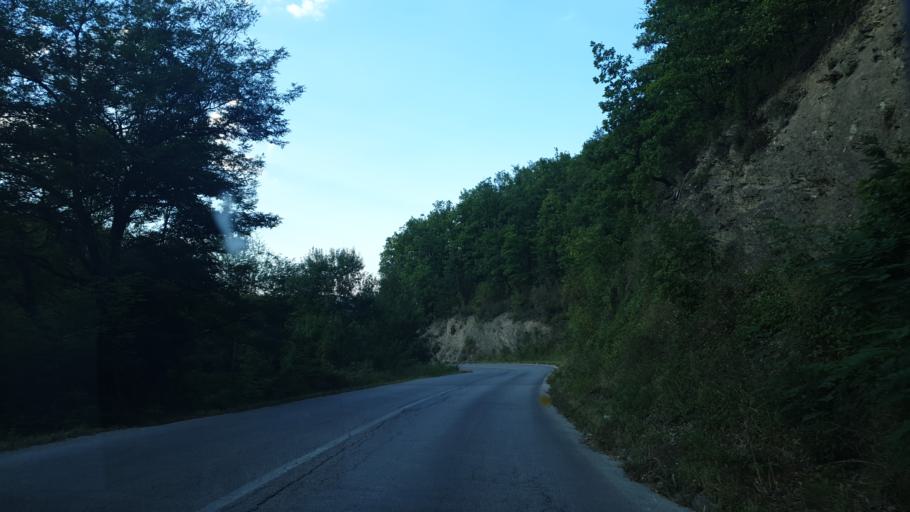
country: RS
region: Central Serbia
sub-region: Zlatiborski Okrug
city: Uzice
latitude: 43.8665
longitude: 19.9059
